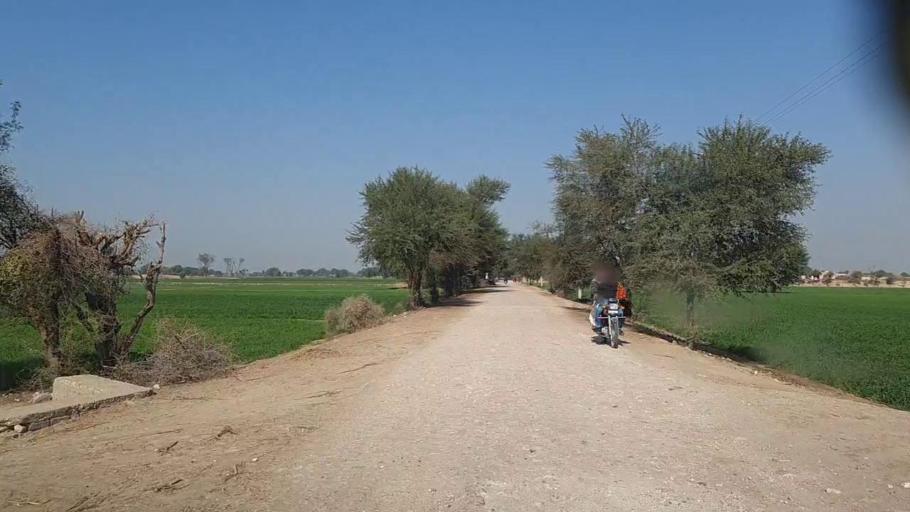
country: PK
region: Sindh
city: Khairpur
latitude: 28.0011
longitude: 69.8498
